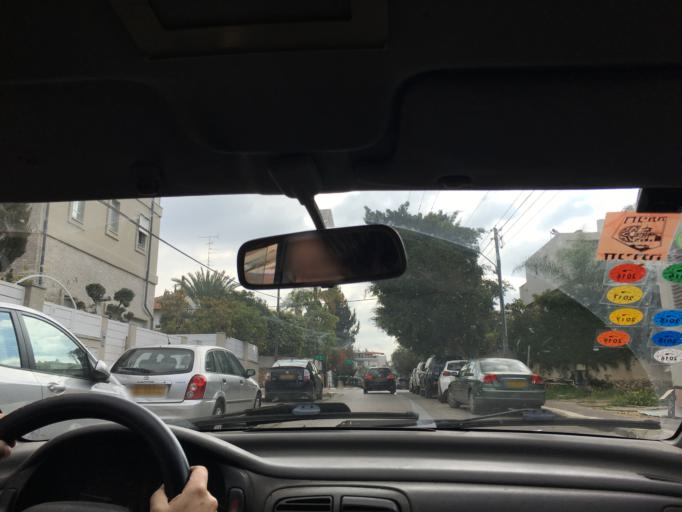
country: IL
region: Tel Aviv
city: Ramat HaSharon
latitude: 32.1421
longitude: 34.8344
